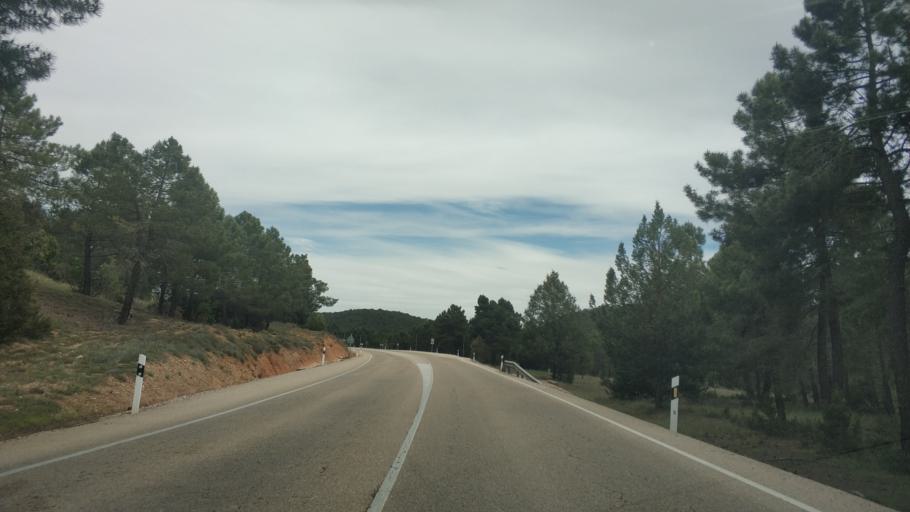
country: ES
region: Castille and Leon
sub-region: Provincia de Soria
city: Bayubas de Abajo
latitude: 41.5129
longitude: -2.9258
